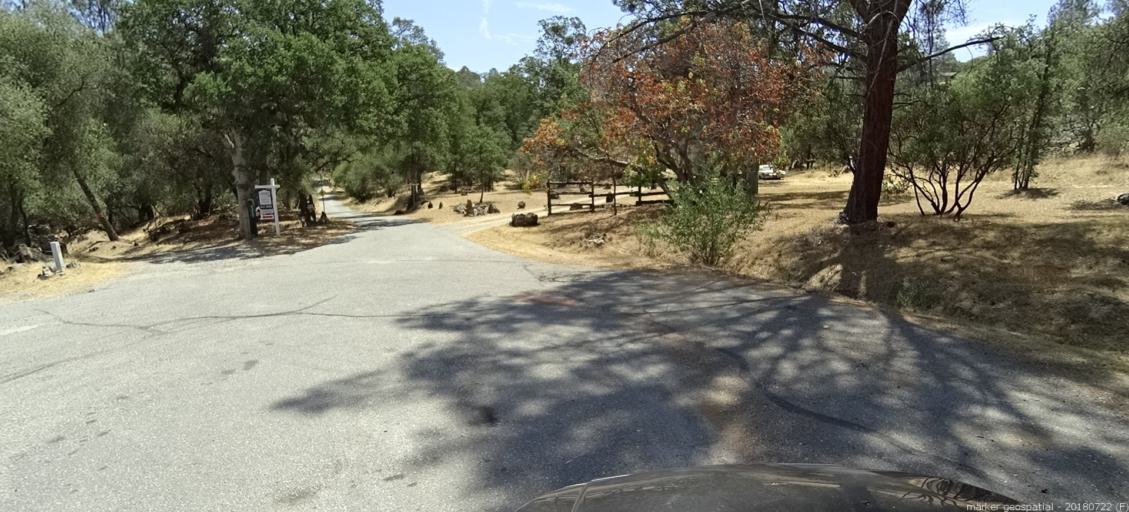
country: US
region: California
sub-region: Madera County
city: Coarsegold
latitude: 37.2806
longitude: -119.7572
